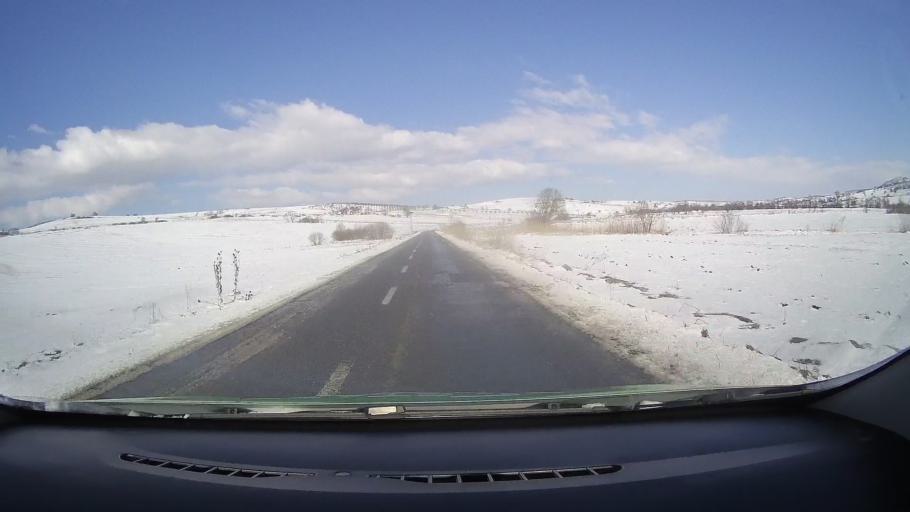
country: RO
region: Sibiu
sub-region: Comuna Vurpar
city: Vurpar
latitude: 45.8704
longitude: 24.3183
